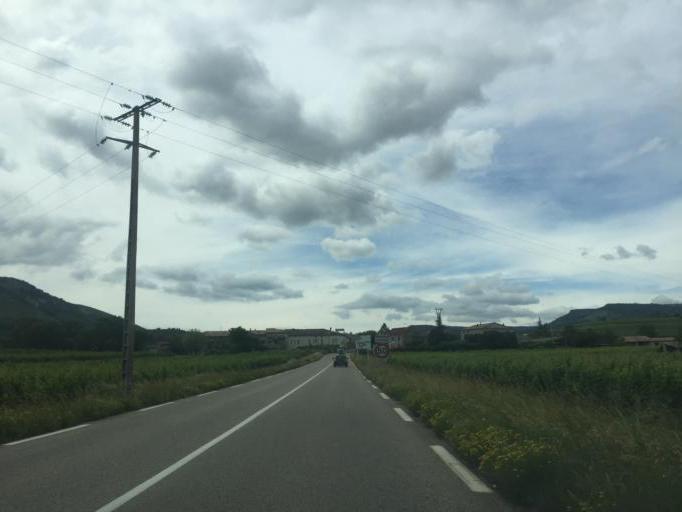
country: FR
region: Rhone-Alpes
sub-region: Departement de l'Ardeche
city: Alba-la-Romaine
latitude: 44.5647
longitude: 4.5925
